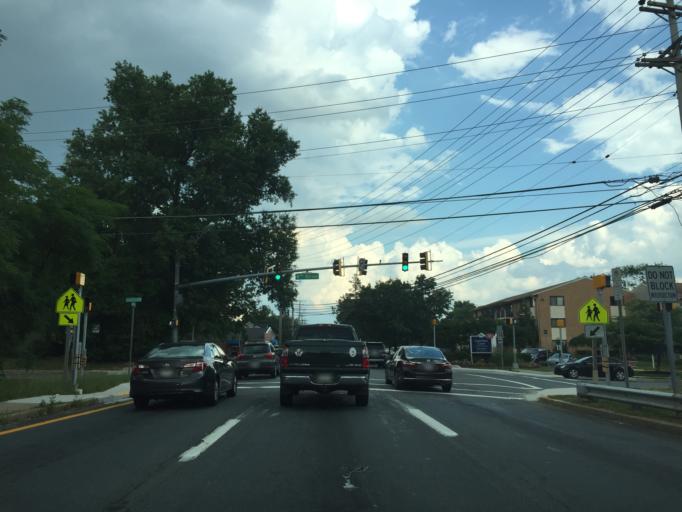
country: US
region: Maryland
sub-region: Prince George's County
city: Laurel
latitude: 39.1015
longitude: -76.8580
